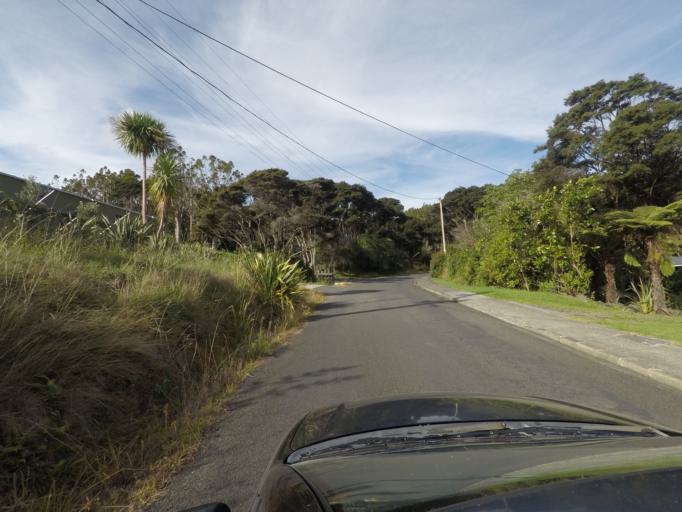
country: NZ
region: Auckland
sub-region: Auckland
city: Titirangi
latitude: -36.9973
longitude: 174.5733
